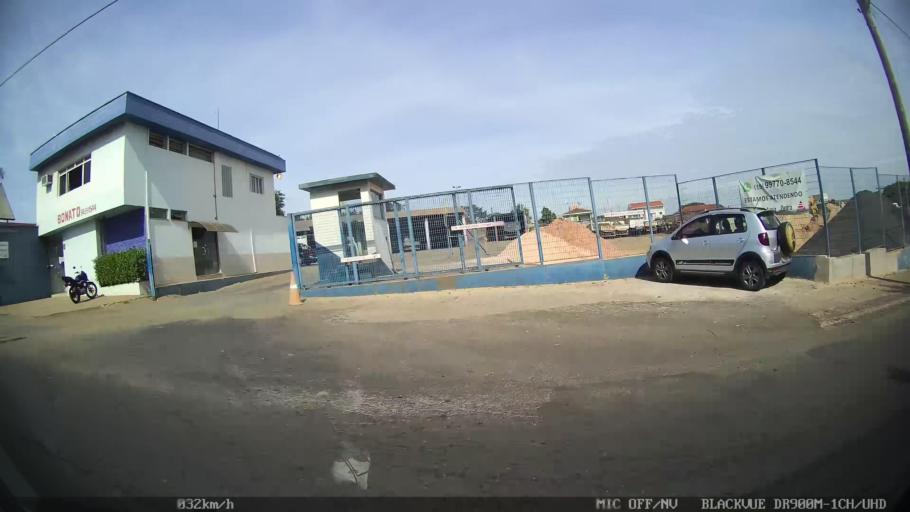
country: BR
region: Sao Paulo
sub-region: Piracicaba
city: Piracicaba
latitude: -22.7336
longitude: -47.6589
